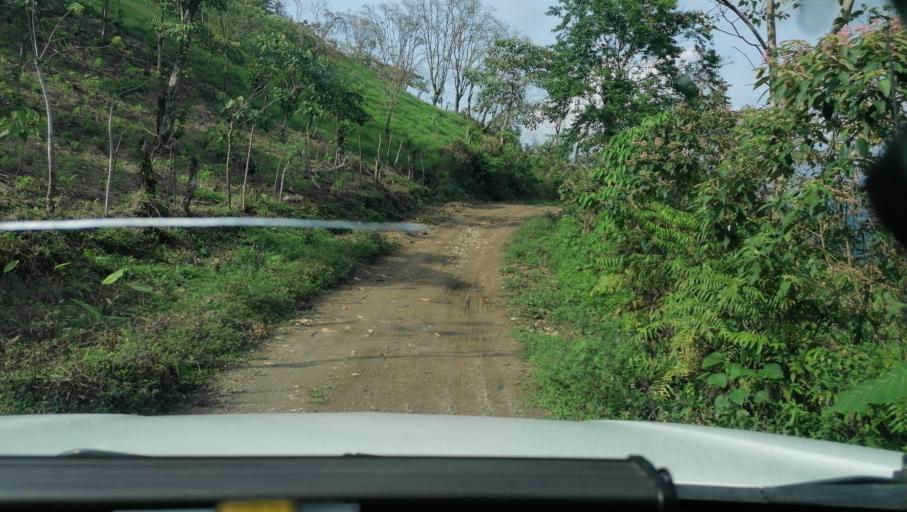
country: MX
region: Chiapas
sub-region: Tapilula
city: San Francisco Jacona
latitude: 17.3044
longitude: -93.1032
